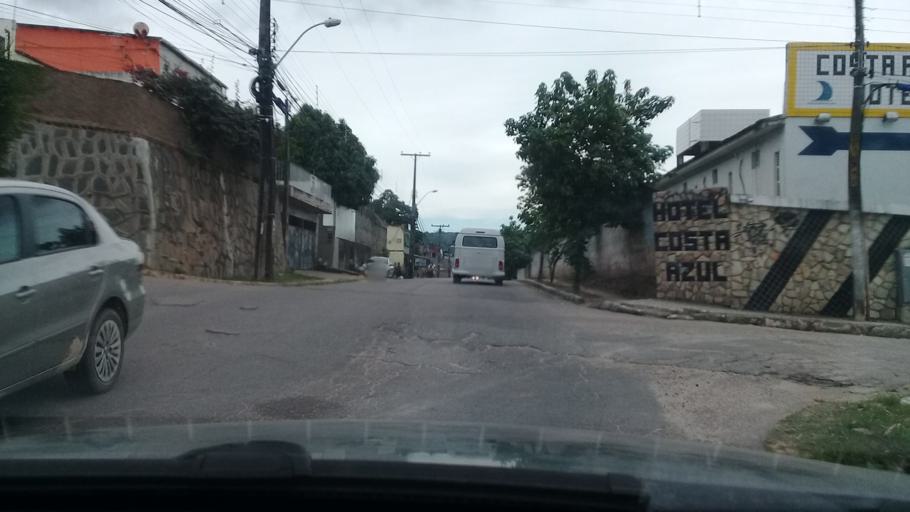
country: BR
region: Pernambuco
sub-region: Sao Lourenco Da Mata
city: Sao Lourenco da Mata
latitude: -8.0333
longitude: -34.9602
